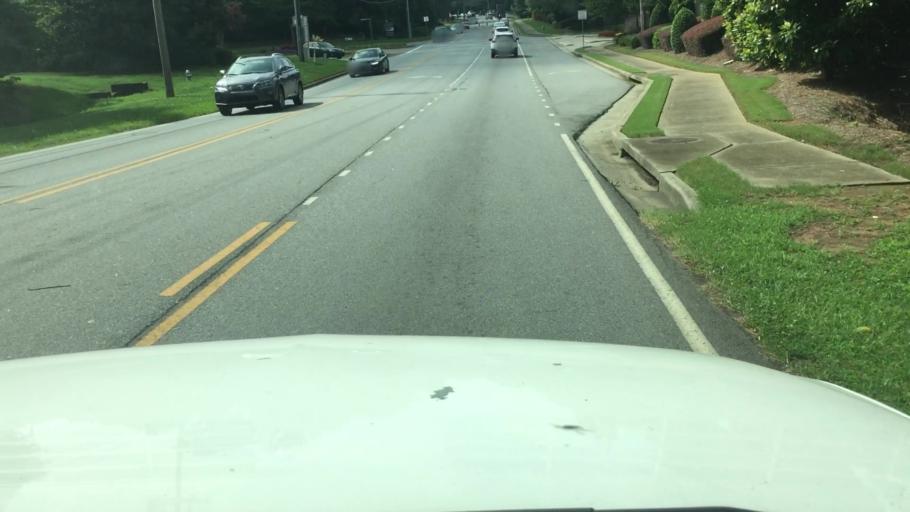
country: US
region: Georgia
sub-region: Fulton County
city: Johns Creek
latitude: 34.0972
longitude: -84.2116
